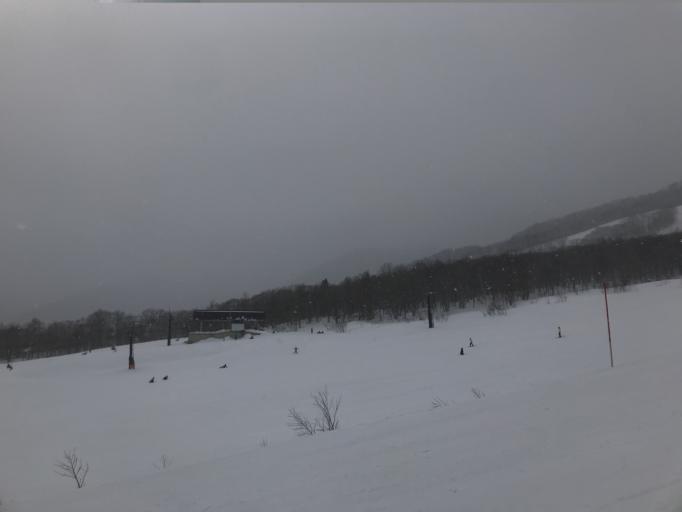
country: JP
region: Nagano
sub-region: Kitaazumi Gun
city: Hakuba
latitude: 36.7585
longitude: 137.8628
